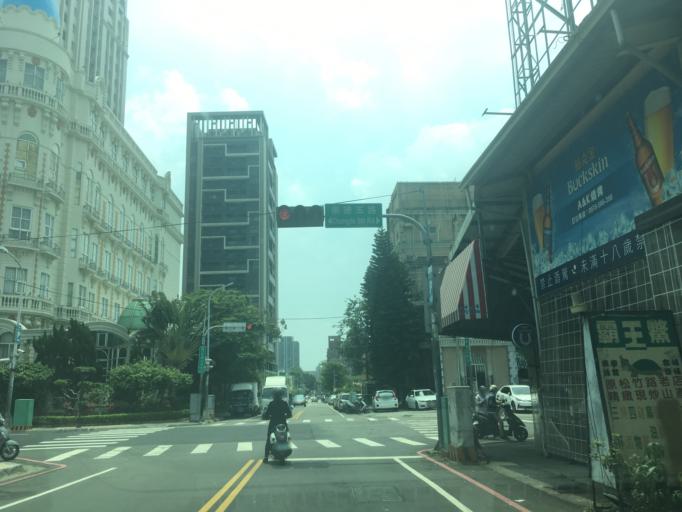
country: TW
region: Taiwan
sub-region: Taichung City
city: Taichung
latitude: 24.1795
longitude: 120.6838
